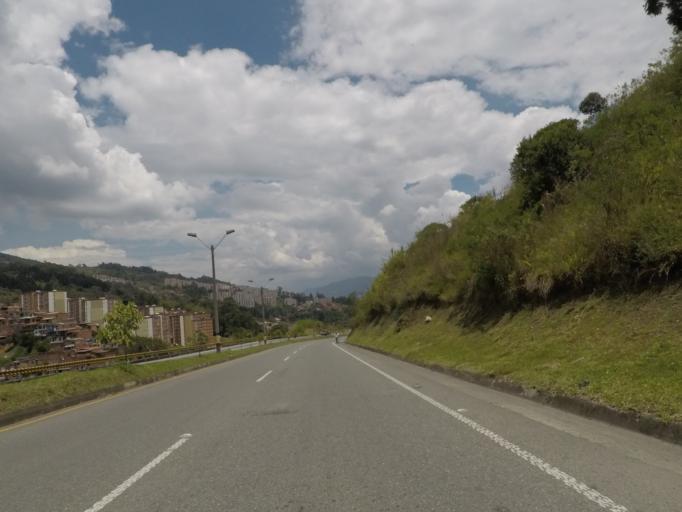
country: CO
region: Antioquia
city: Medellin
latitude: 6.2754
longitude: -75.6324
